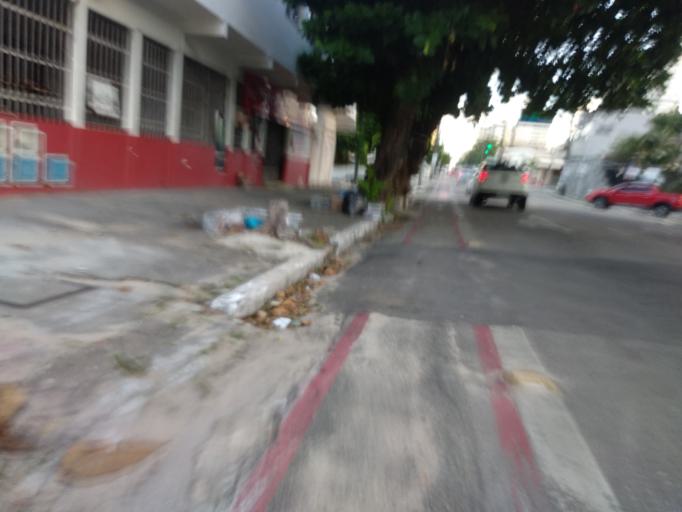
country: BR
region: Ceara
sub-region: Fortaleza
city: Fortaleza
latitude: -3.7376
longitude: -38.5099
